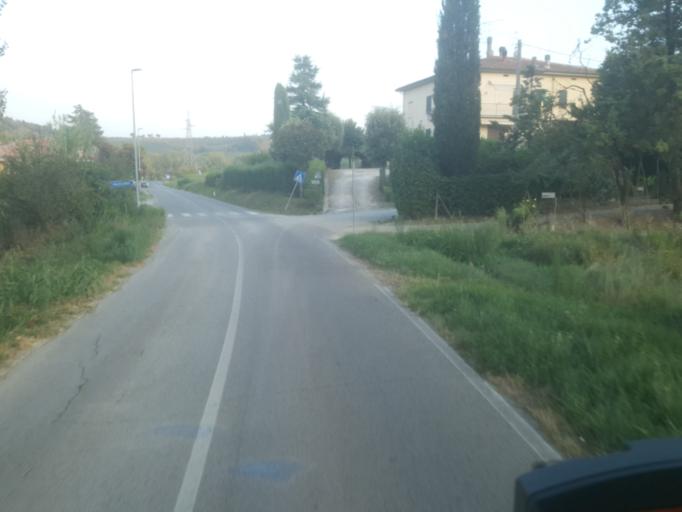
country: IT
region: Tuscany
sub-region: Province of Florence
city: Certaldo
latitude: 43.5328
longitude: 11.0342
